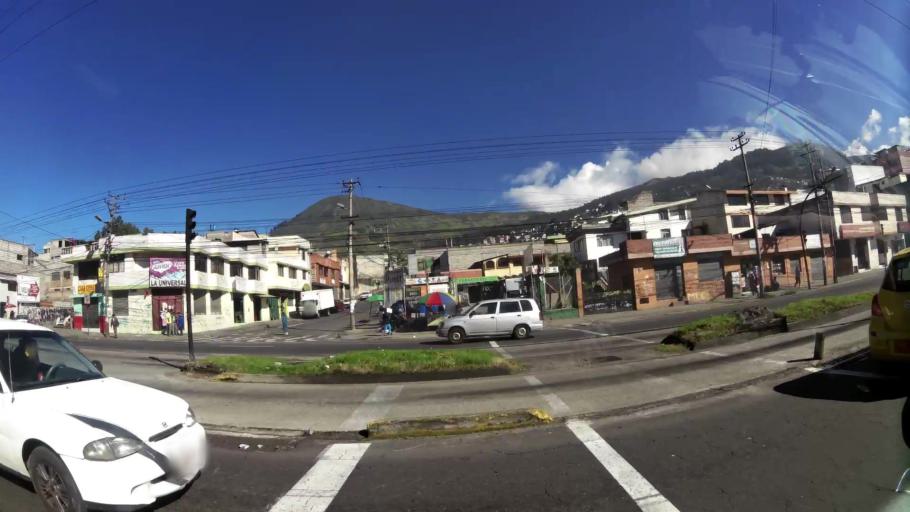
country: EC
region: Pichincha
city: Quito
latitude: -0.2419
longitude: -78.5323
